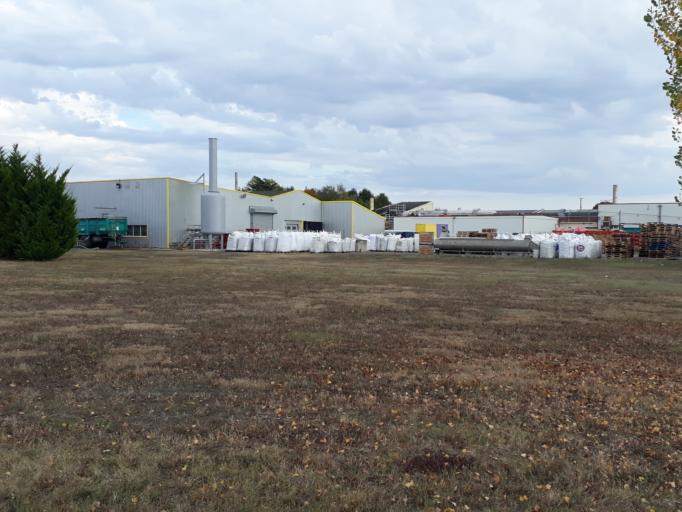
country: FR
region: Centre
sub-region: Departement du Loiret
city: Saint-Benoit-sur-Loire
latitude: 47.7944
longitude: 2.3106
